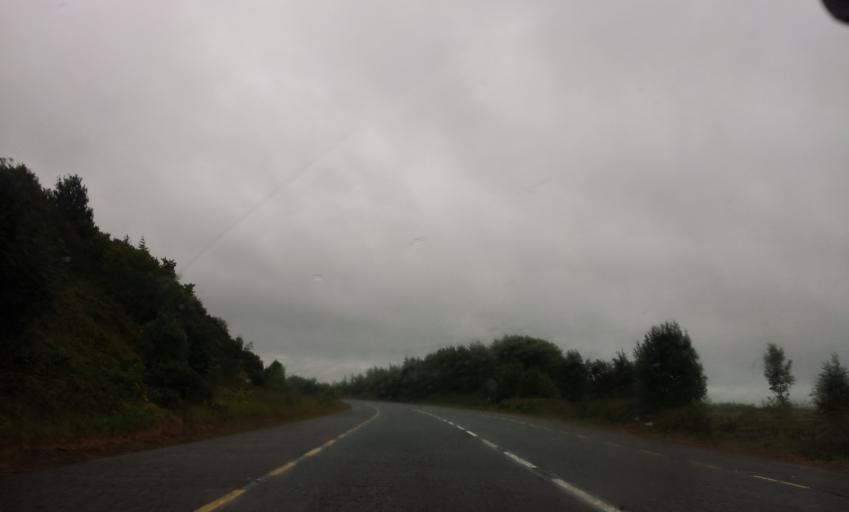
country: IE
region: Munster
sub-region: County Cork
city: Blarney
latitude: 51.9634
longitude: -8.5760
